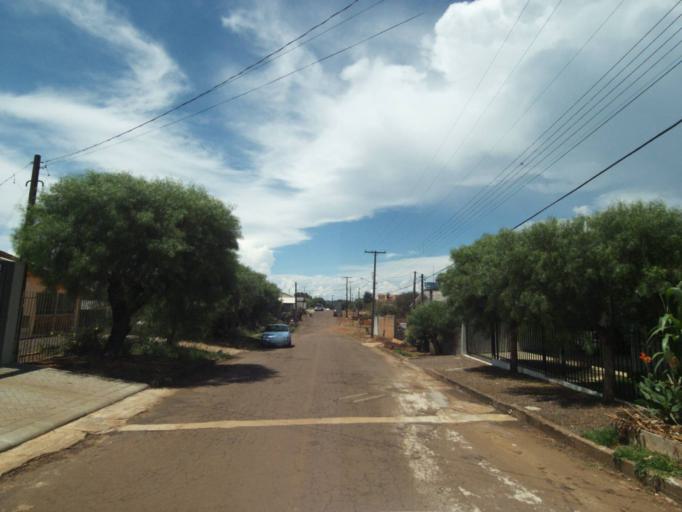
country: BR
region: Parana
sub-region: Guaraniacu
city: Guaraniacu
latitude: -25.0952
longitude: -52.8765
